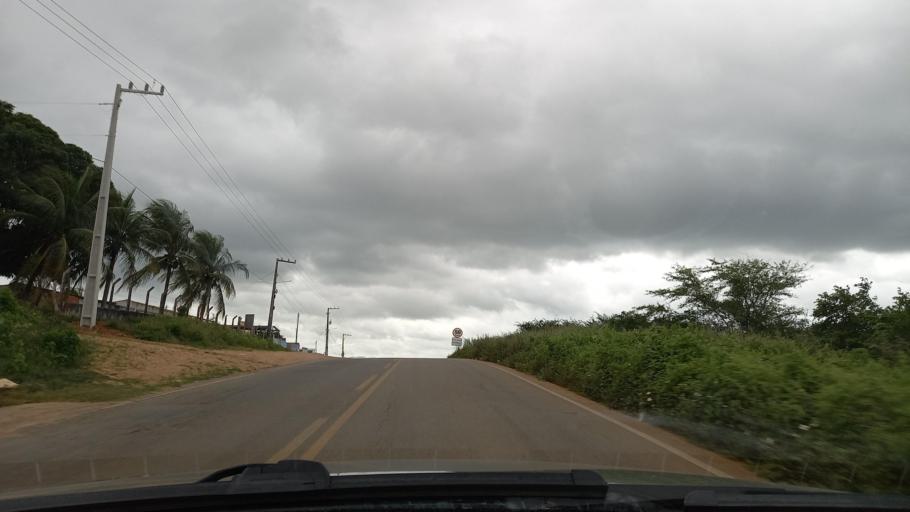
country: BR
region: Sergipe
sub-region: Caninde De Sao Francisco
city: Caninde de Sao Francisco
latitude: -9.6708
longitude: -37.7988
